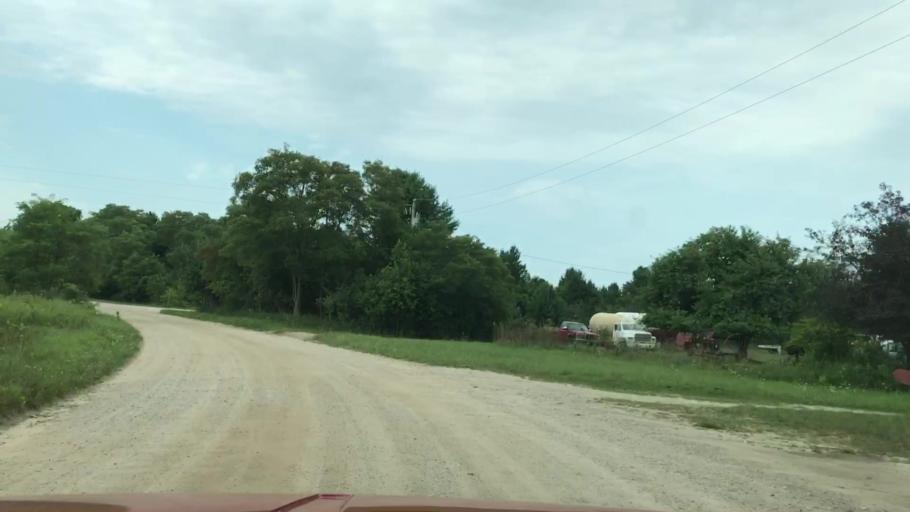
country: US
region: Michigan
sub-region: Charlevoix County
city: Charlevoix
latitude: 45.7216
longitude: -85.5569
